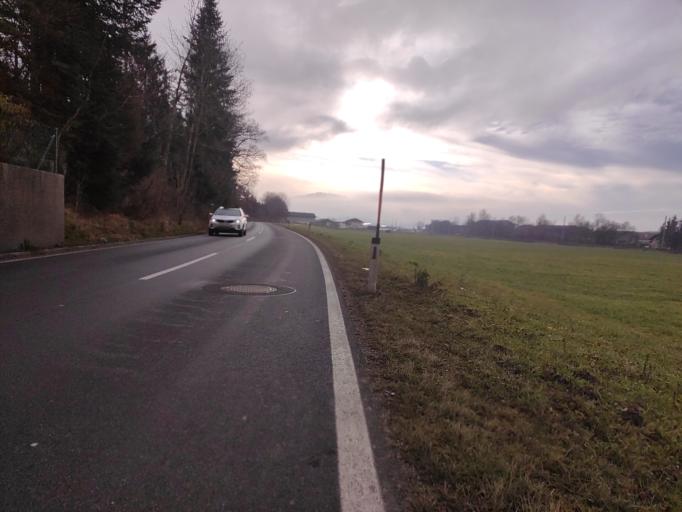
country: AT
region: Salzburg
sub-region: Politischer Bezirk Salzburg-Umgebung
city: Strasswalchen
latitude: 47.9939
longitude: 13.2409
